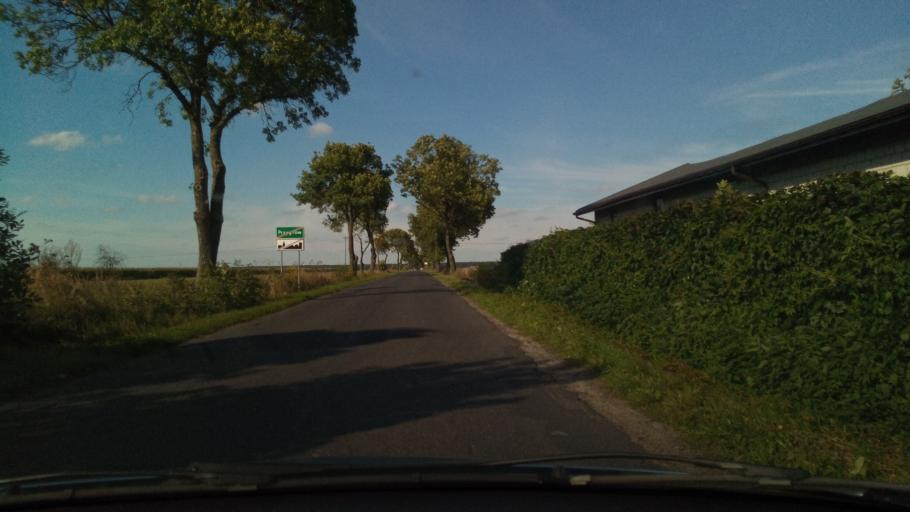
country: PL
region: Lodz Voivodeship
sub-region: Powiat piotrkowski
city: Sulejow
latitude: 51.3803
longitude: 19.8177
